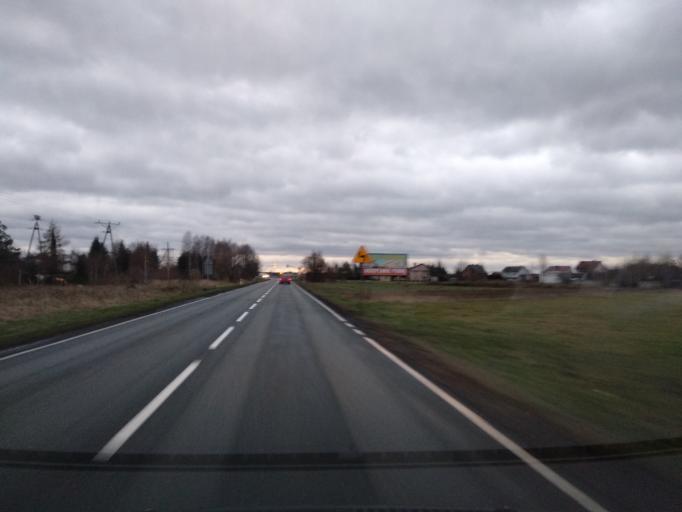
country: PL
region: Greater Poland Voivodeship
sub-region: Powiat koninski
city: Rychwal
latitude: 52.0754
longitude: 18.1591
